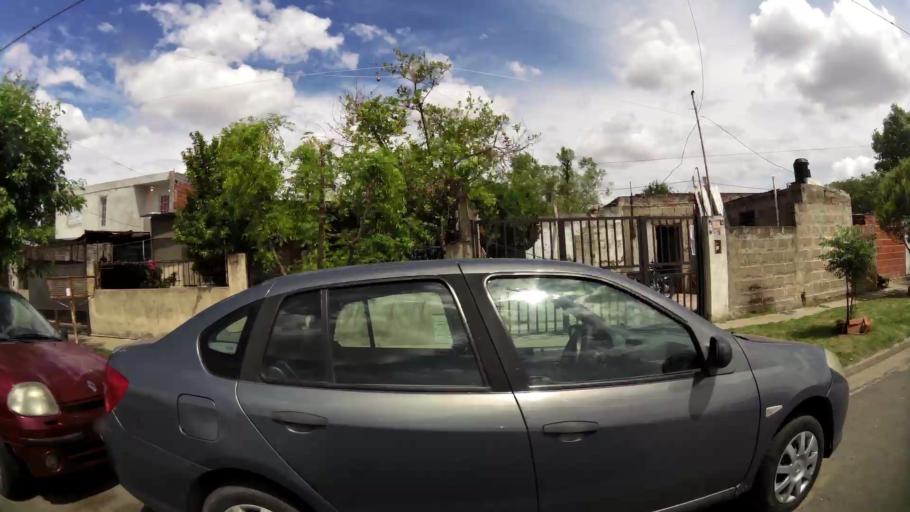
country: AR
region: Santa Fe
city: Gobernador Galvez
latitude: -33.0150
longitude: -60.6437
